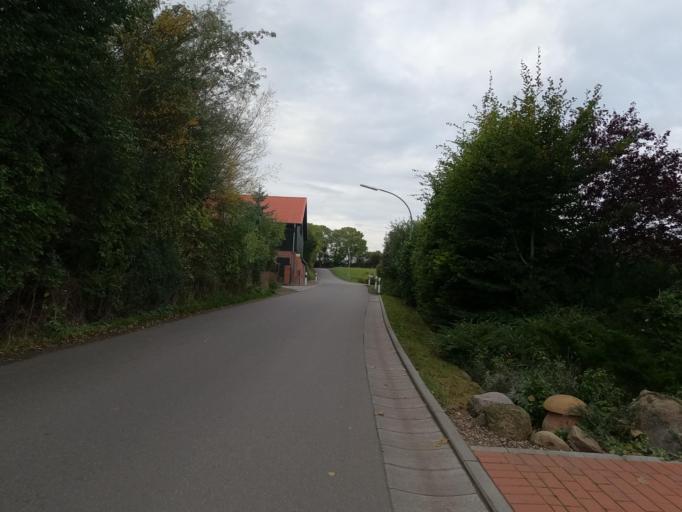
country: DE
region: Schleswig-Holstein
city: Neukirchen
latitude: 54.3251
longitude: 11.0363
